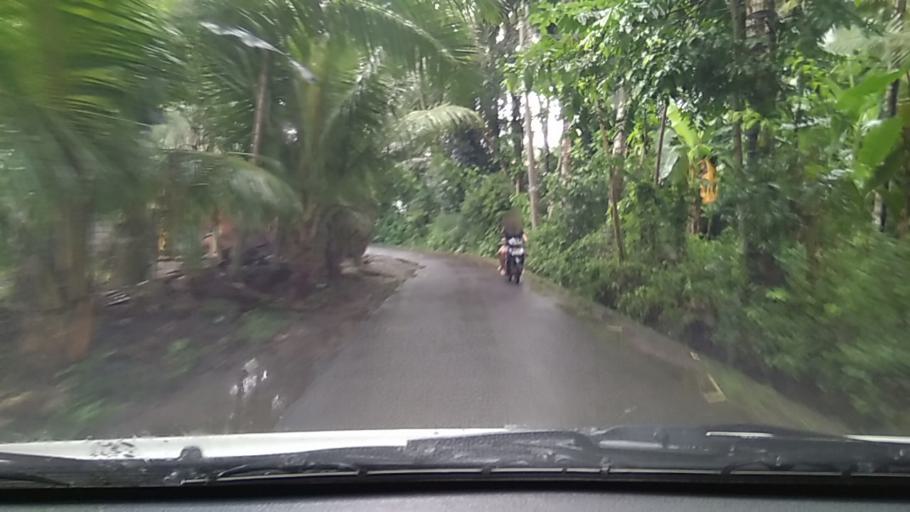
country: ID
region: Bali
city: Banjar Bugbug
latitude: -8.5093
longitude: 115.5789
